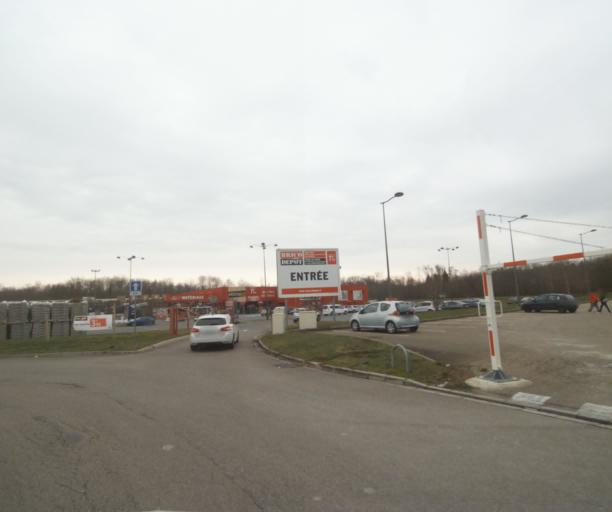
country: FR
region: Champagne-Ardenne
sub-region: Departement de la Haute-Marne
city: Saint-Dizier
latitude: 48.6228
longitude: 4.9693
